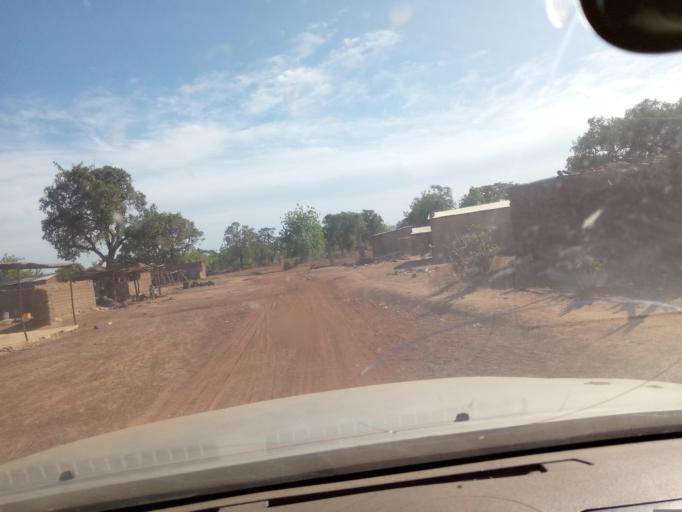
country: ML
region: Sikasso
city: Sikasso
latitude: 11.4789
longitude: -5.3313
